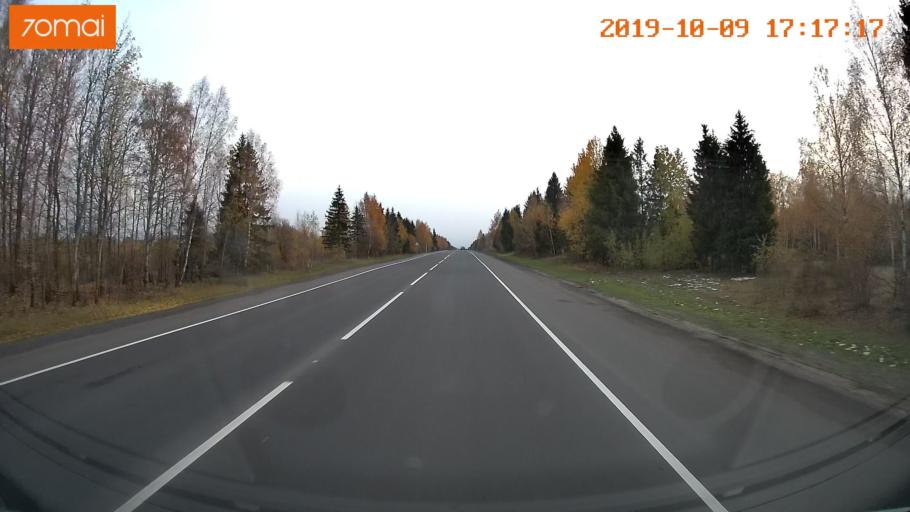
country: RU
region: Ivanovo
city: Furmanov
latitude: 57.2779
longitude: 41.1587
